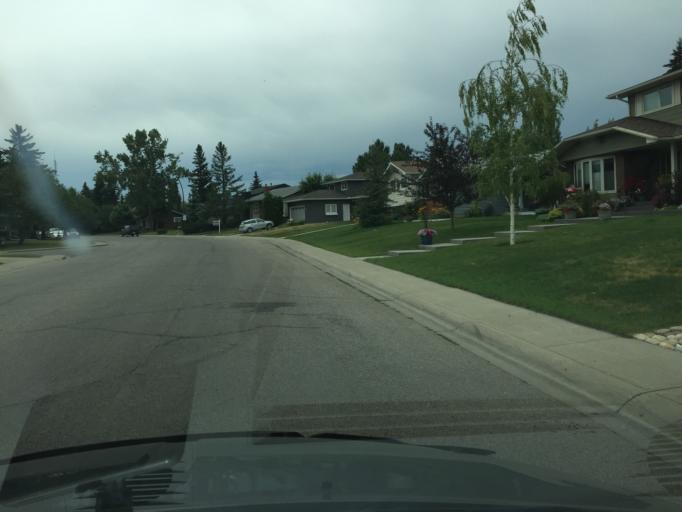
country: CA
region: Alberta
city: Calgary
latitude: 50.9330
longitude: -114.0388
